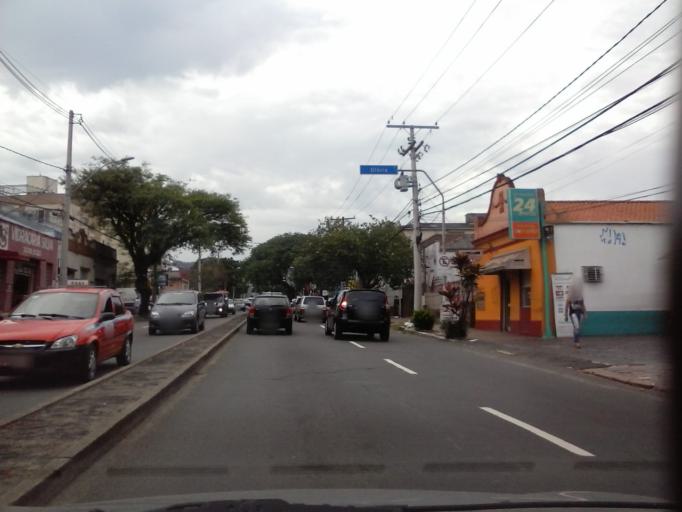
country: BR
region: Rio Grande do Sul
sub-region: Porto Alegre
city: Porto Alegre
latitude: -30.0700
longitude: -51.2047
